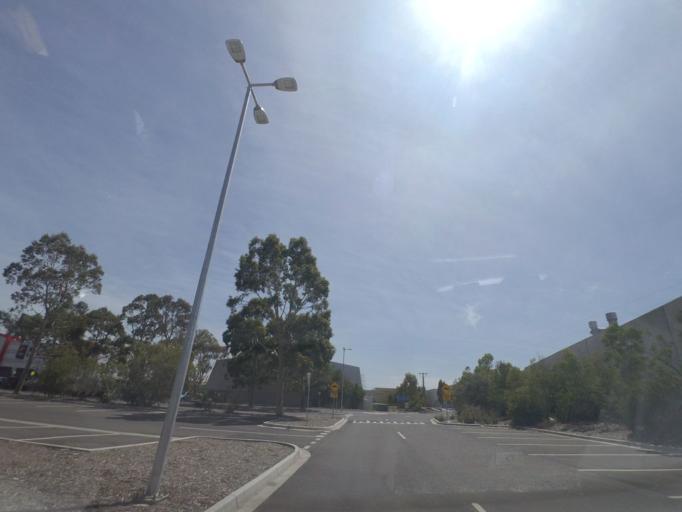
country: AU
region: Victoria
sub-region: Brimbank
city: Keilor Park
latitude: -37.7132
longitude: 144.8495
